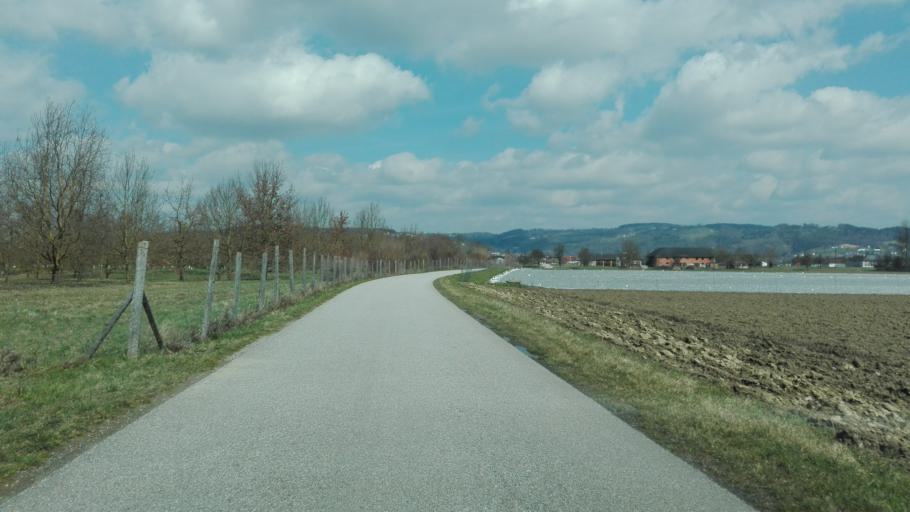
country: AT
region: Upper Austria
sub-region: Politischer Bezirk Urfahr-Umgebung
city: Feldkirchen an der Donau
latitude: 48.3345
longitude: 14.0508
